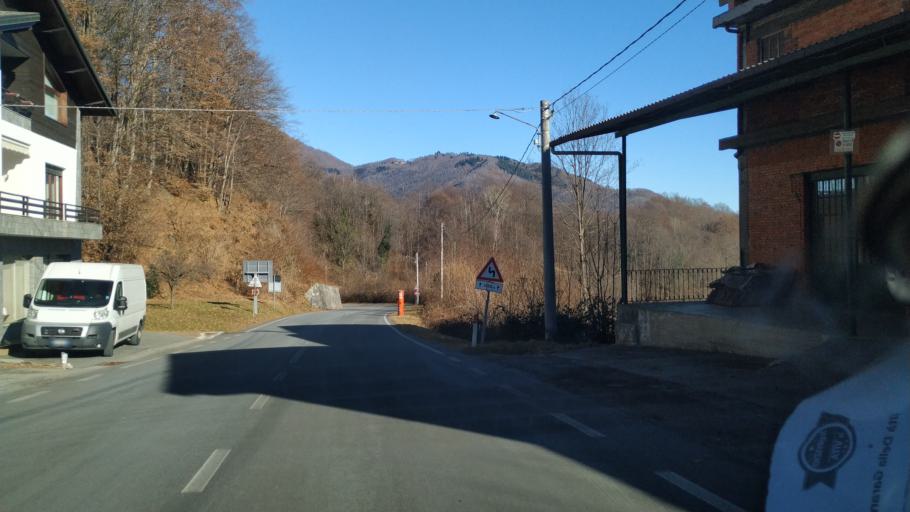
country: IT
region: Piedmont
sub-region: Provincia di Biella
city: Portula
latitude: 45.6761
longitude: 8.1771
